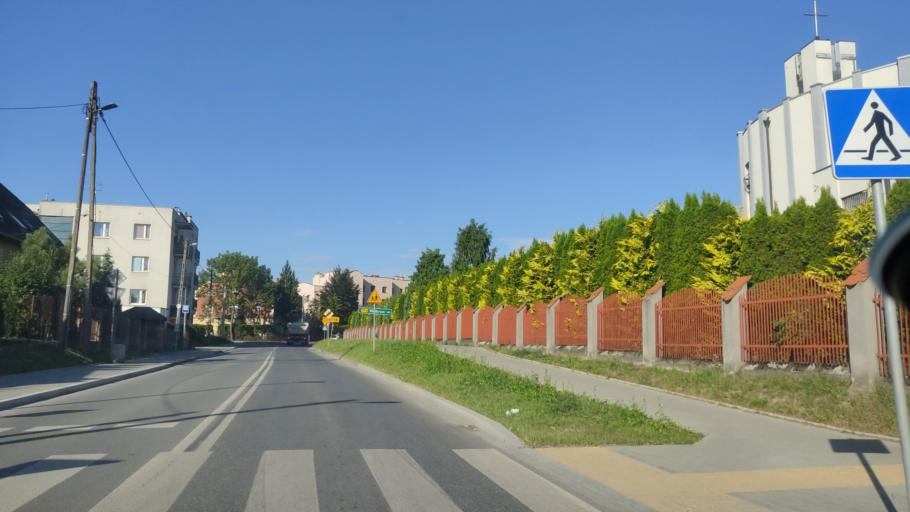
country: PL
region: Lesser Poland Voivodeship
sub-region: Powiat krakowski
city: Zielonki
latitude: 50.0967
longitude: 19.9332
